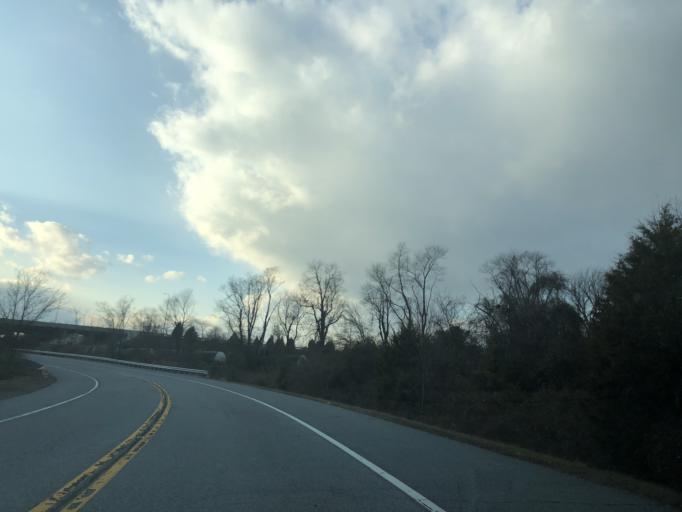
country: US
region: Delaware
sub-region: New Castle County
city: Bear
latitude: 39.6322
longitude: -75.6508
